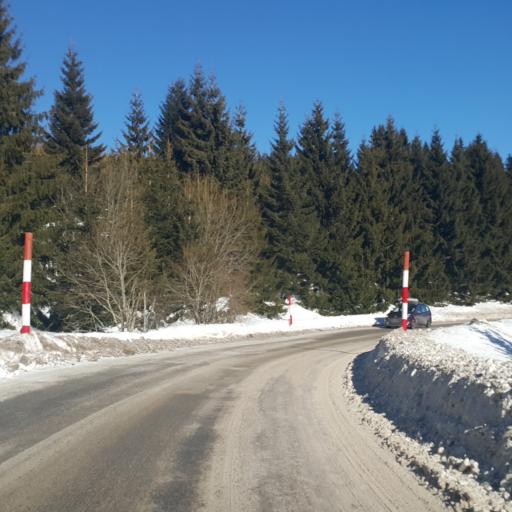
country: XK
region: Mitrovica
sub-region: Komuna e Leposaviqit
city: Leposaviq
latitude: 43.3224
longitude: 20.8442
